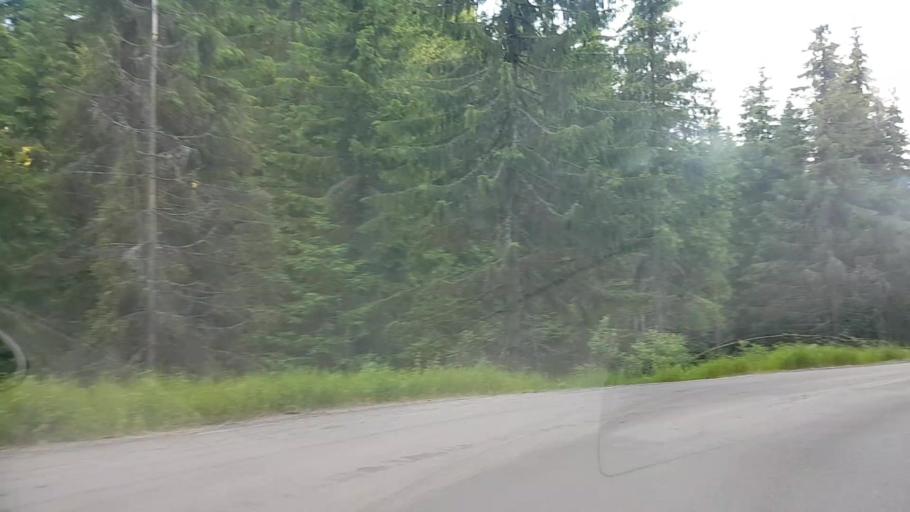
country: RO
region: Harghita
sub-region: Comuna Varsag
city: Varsag
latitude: 46.6463
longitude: 25.2879
